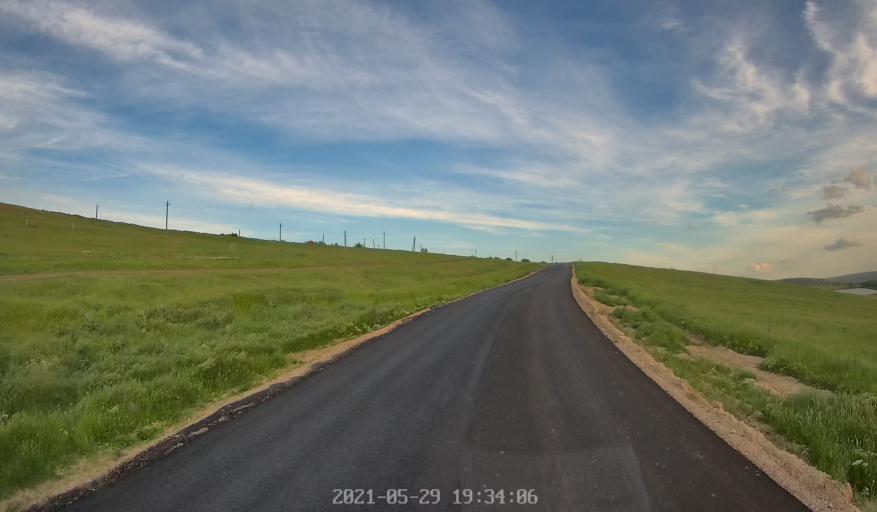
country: MD
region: Chisinau
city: Singera
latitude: 46.8284
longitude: 28.9589
